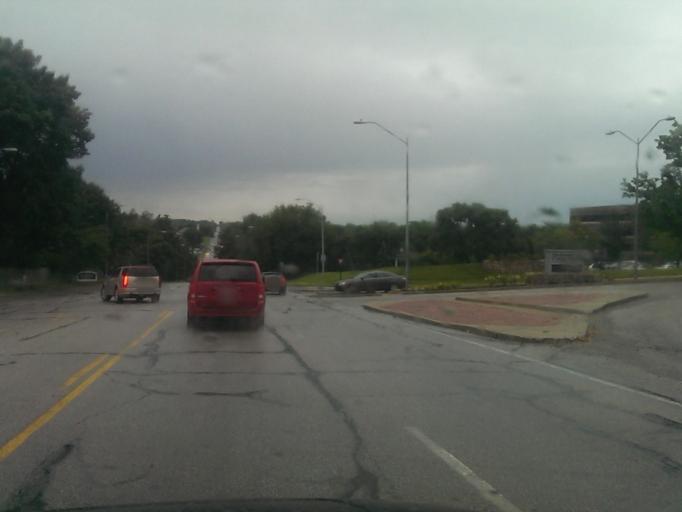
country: US
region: Kansas
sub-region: Johnson County
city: Leawood
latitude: 38.9430
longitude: -94.5826
